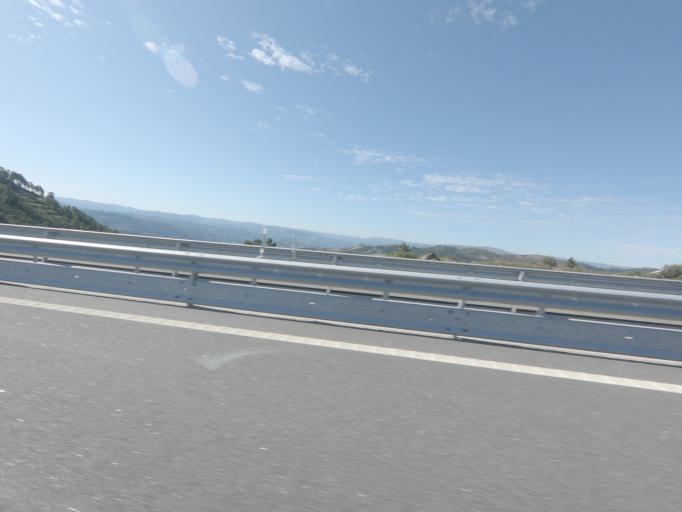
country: PT
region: Vila Real
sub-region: Santa Marta de Penaguiao
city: Santa Marta de Penaguiao
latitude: 41.2648
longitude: -7.8011
